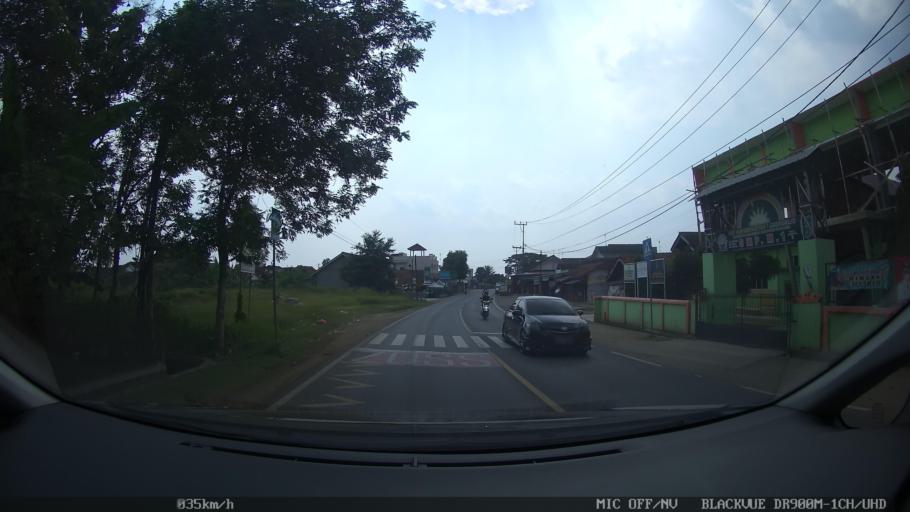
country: ID
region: Lampung
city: Gadingrejo
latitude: -5.3751
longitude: 105.0639
